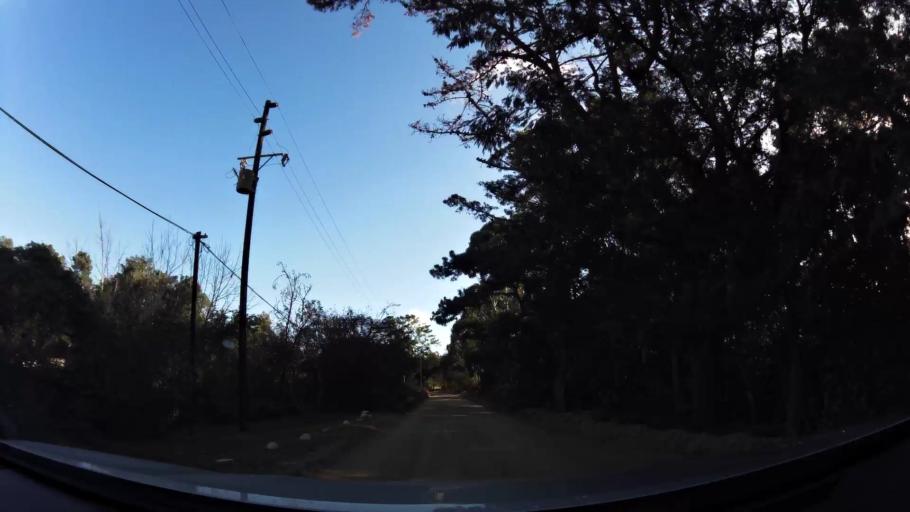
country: ZA
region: Western Cape
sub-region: Eden District Municipality
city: George
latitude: -33.9807
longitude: 22.5705
